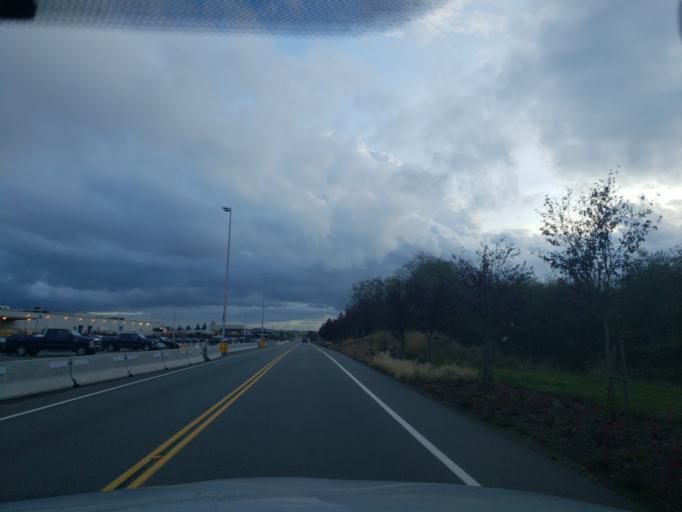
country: US
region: Washington
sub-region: Snohomish County
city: Mukilteo
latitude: 47.9321
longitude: -122.2848
